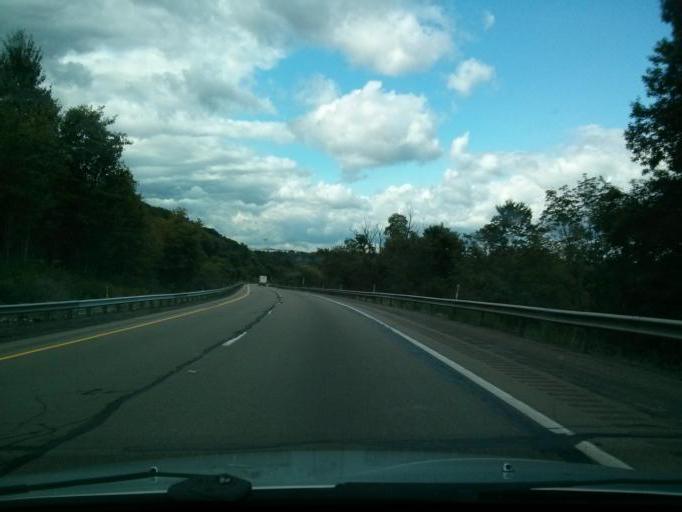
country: US
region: Pennsylvania
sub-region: Jefferson County
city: Brookville
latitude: 41.1707
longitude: -79.0177
